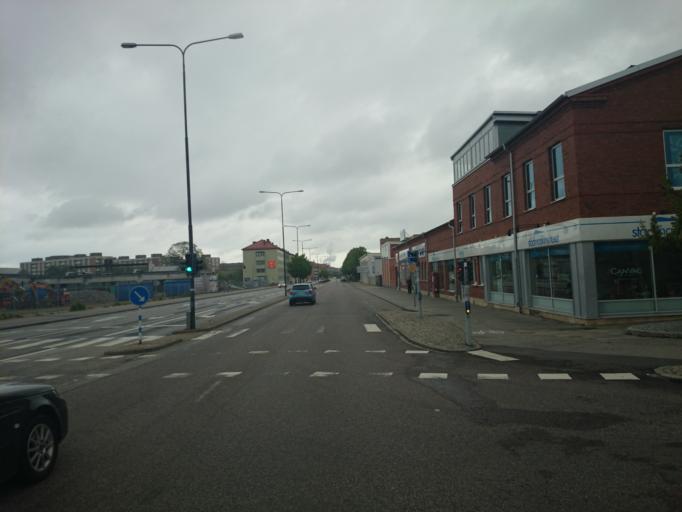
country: SE
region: Skane
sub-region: Malmo
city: Malmoe
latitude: 55.5994
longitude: 13.0253
